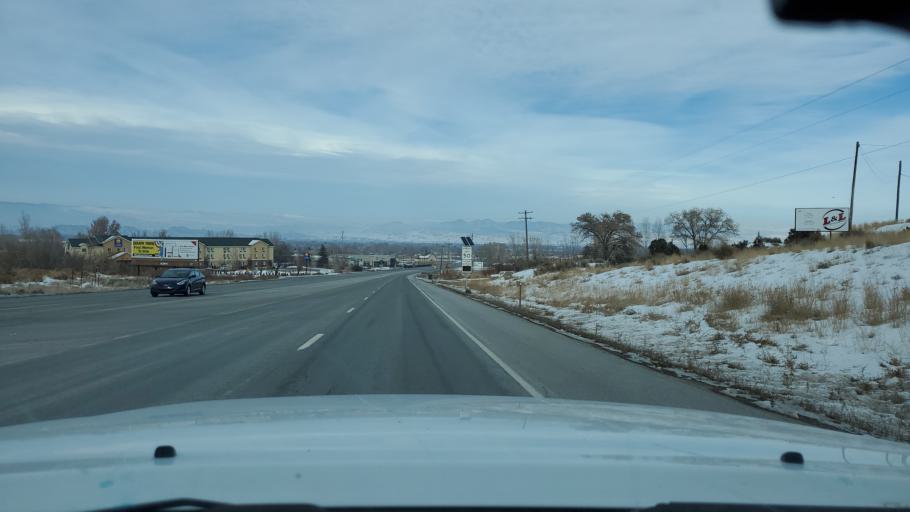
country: US
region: Utah
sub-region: Uintah County
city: Maeser
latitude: 40.4302
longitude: -109.5758
